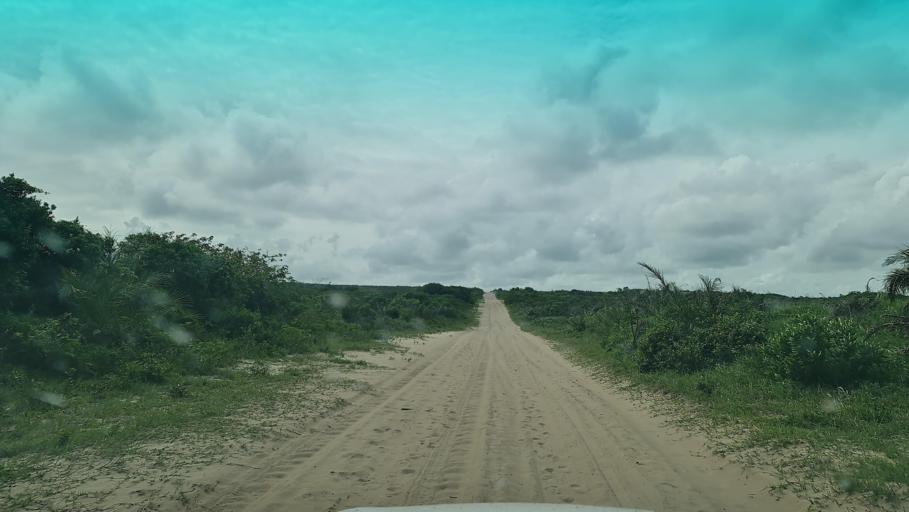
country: MZ
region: Maputo
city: Manhica
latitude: -25.4507
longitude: 32.9547
